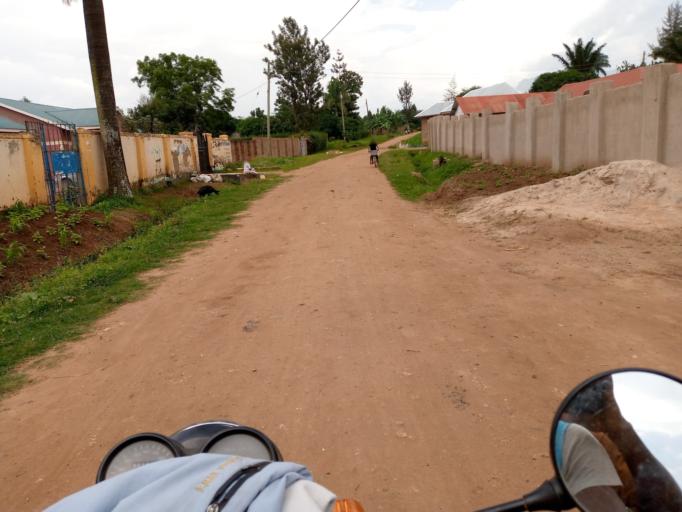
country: UG
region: Eastern Region
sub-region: Mbale District
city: Mbale
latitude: 1.0882
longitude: 34.1676
